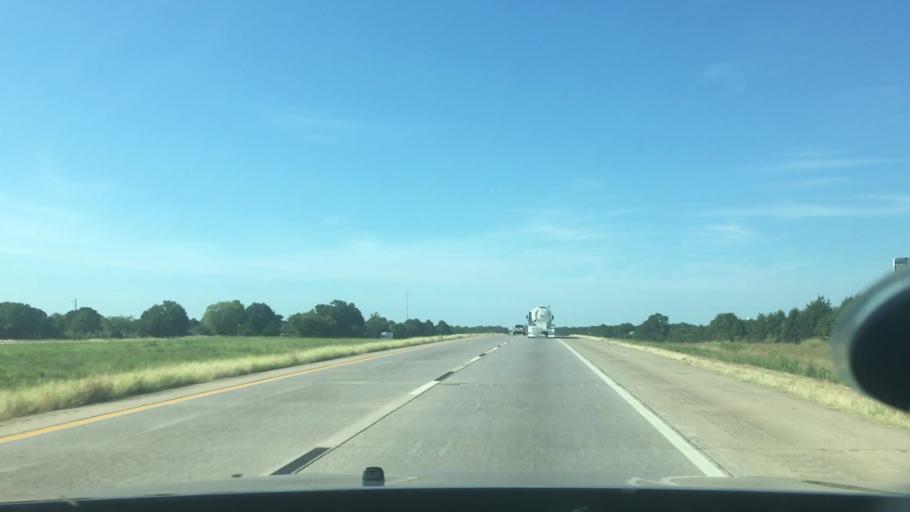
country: US
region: Oklahoma
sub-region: Atoka County
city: Atoka
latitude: 34.1970
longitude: -96.2405
